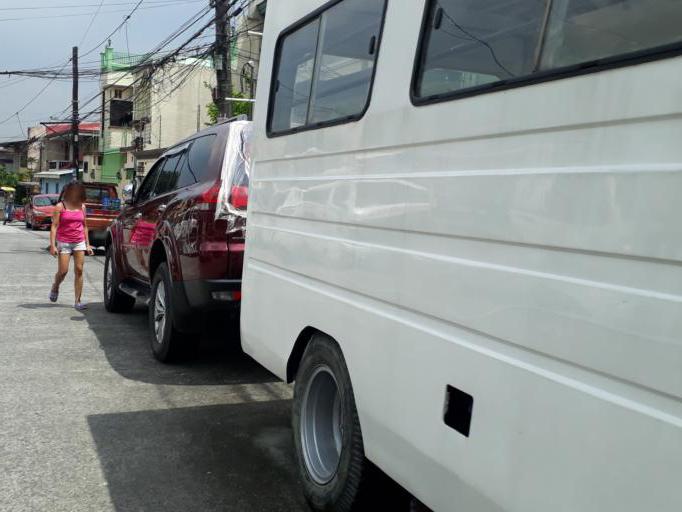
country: PH
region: Calabarzon
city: Bagong Pagasa
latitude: 14.6636
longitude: 121.0347
